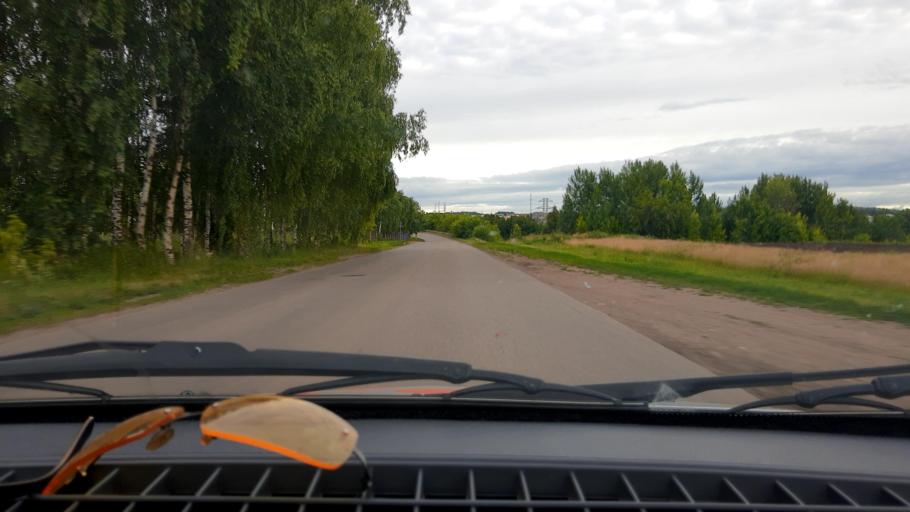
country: RU
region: Bashkortostan
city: Chishmy
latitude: 54.5996
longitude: 55.4428
